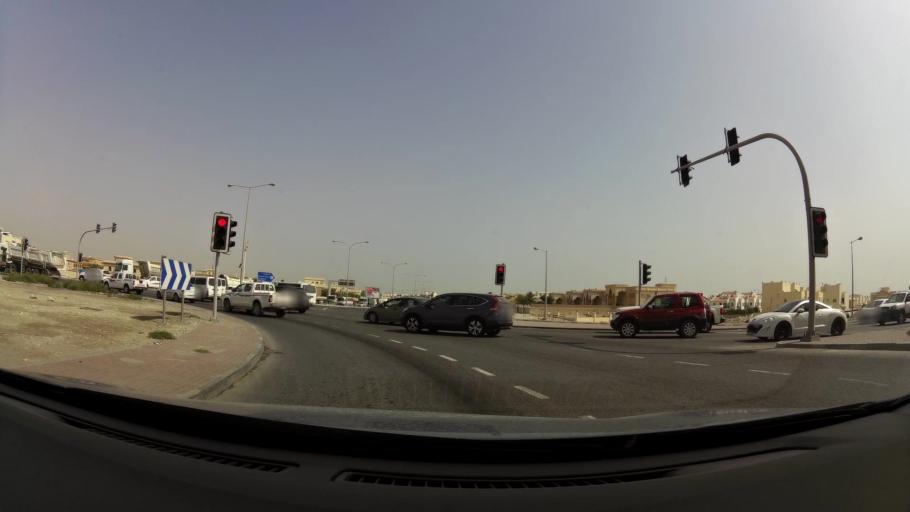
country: QA
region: Baladiyat ad Dawhah
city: Doha
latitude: 25.2376
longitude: 51.5232
